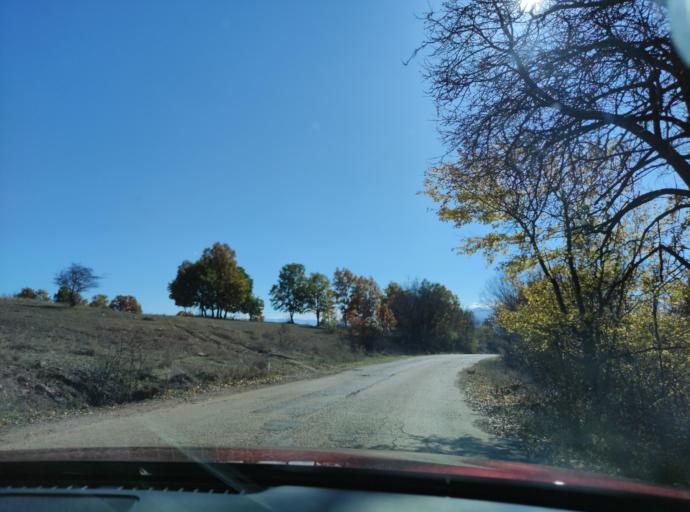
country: BG
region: Montana
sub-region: Obshtina Chiprovtsi
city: Chiprovtsi
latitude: 43.4471
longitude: 23.0476
